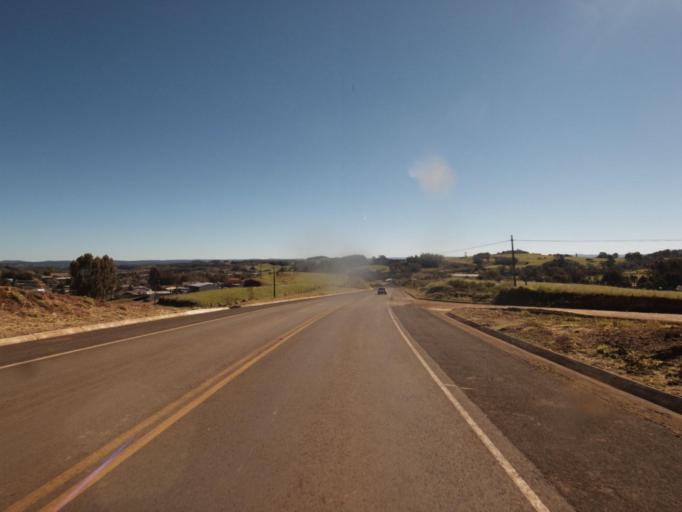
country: AR
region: Misiones
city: Bernardo de Irigoyen
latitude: -26.6151
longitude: -53.6689
